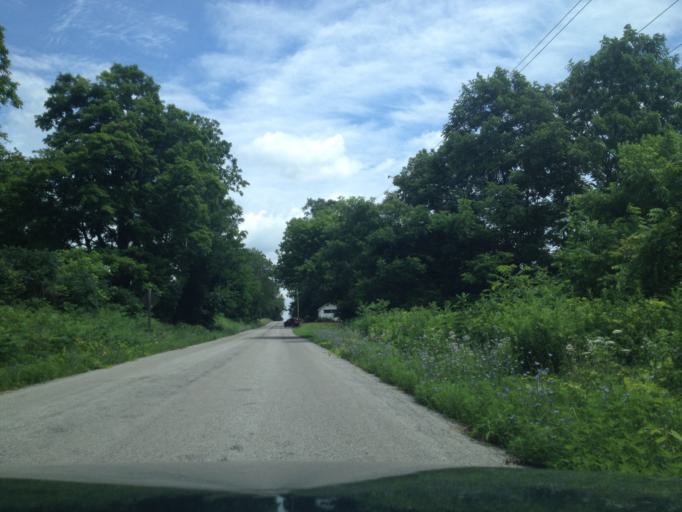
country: CA
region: Ontario
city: Norfolk County
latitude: 42.7812
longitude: -80.2965
